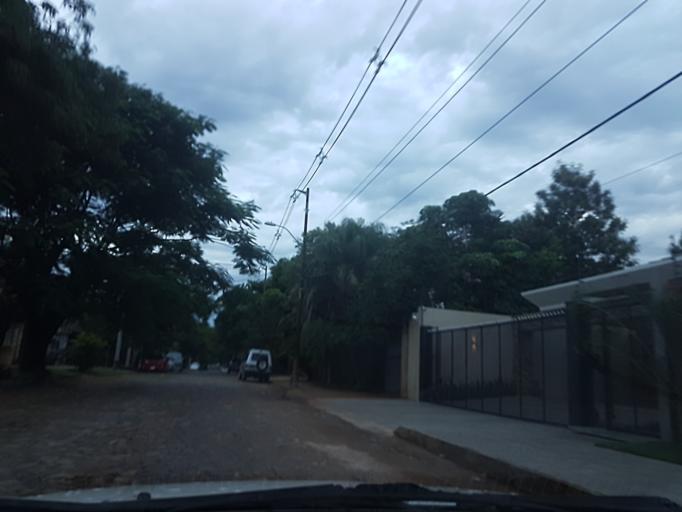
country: PY
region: Asuncion
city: Asuncion
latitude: -25.2835
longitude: -57.5975
